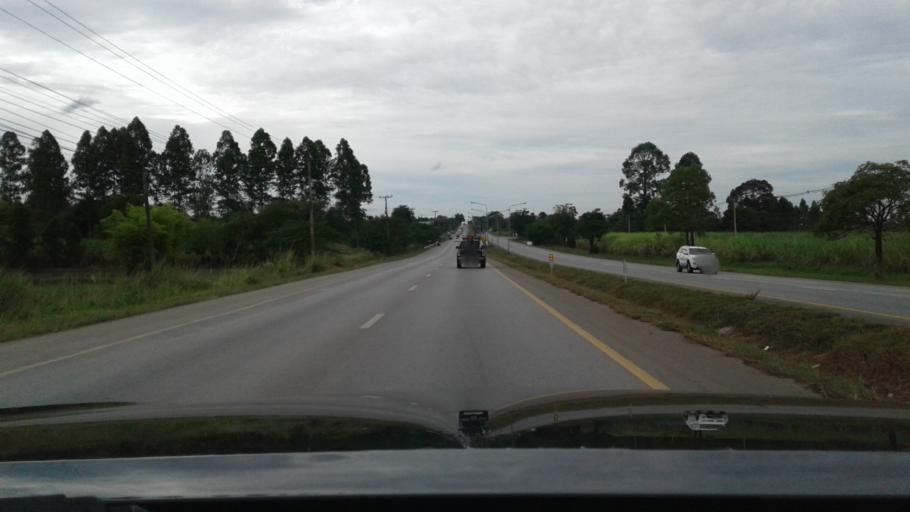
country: TH
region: Changwat Udon Thani
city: Non Sa-at
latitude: 17.0377
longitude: 102.9109
